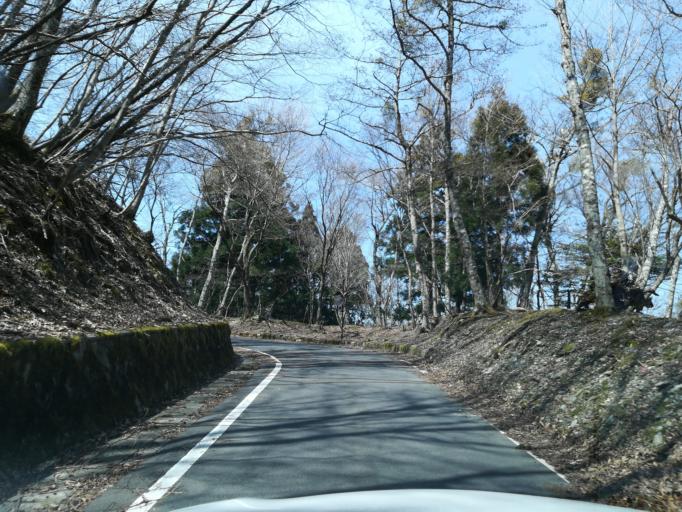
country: JP
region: Tokushima
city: Wakimachi
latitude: 33.8824
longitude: 134.0611
